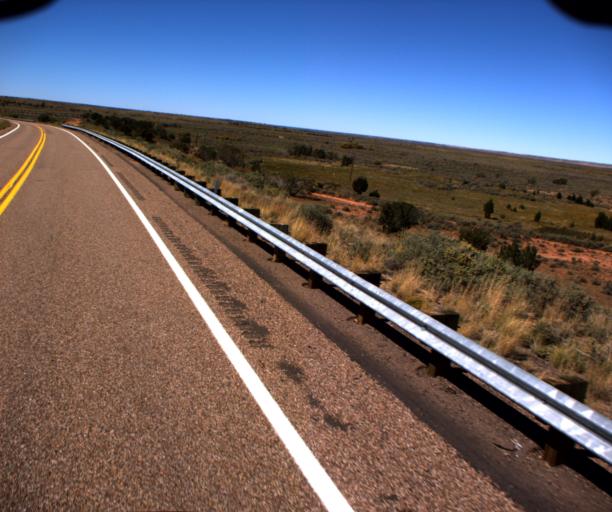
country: US
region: Arizona
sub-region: Apache County
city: Saint Johns
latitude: 34.5876
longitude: -109.5486
